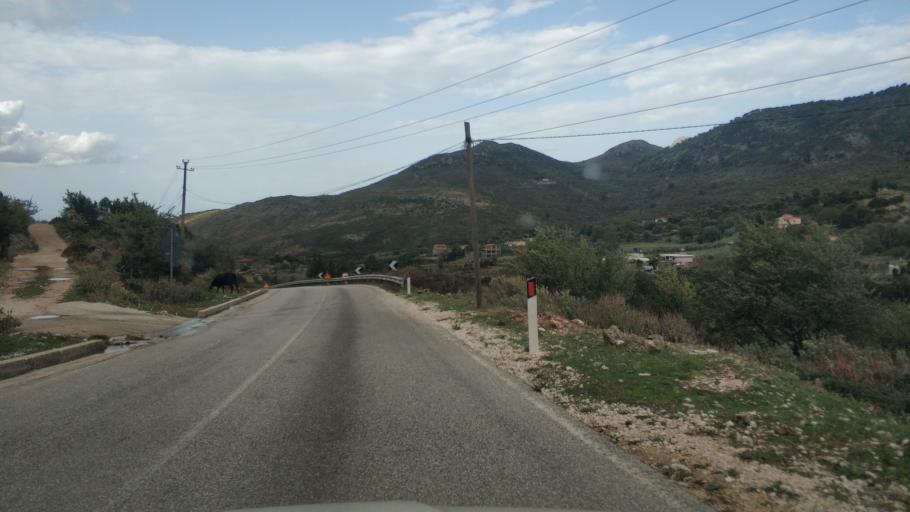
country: AL
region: Vlore
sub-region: Rrethi i Vlores
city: Orikum
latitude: 40.2676
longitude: 19.5157
